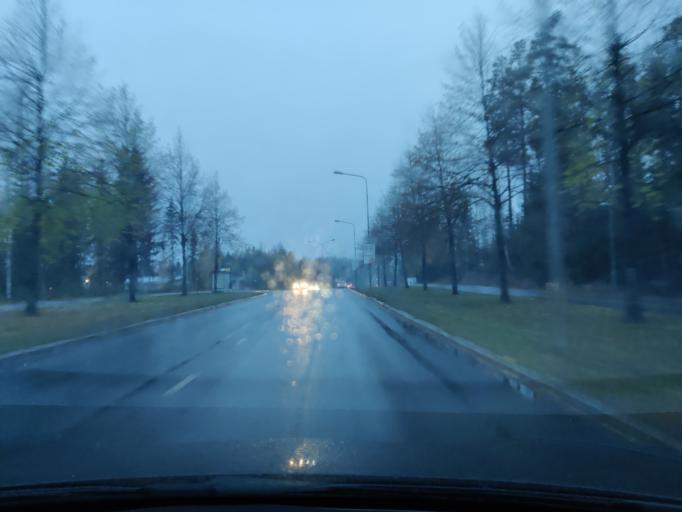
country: FI
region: Northern Savo
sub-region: Kuopio
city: Kuopio
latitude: 62.8357
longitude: 27.6611
